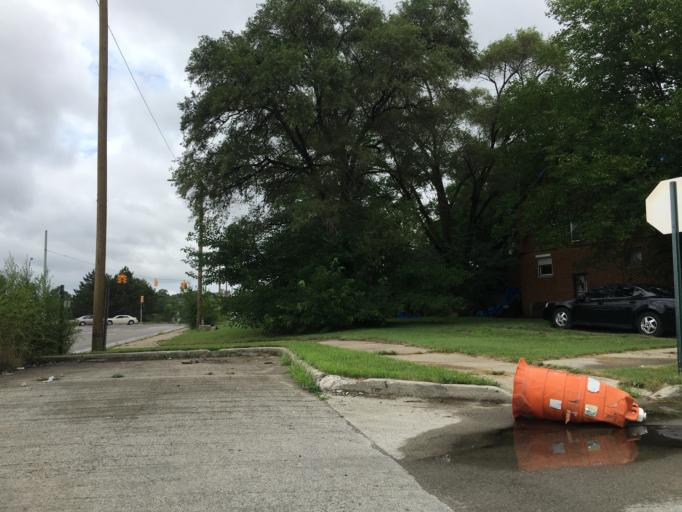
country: US
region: Michigan
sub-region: Oakland County
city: Oak Park
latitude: 42.4054
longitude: -83.1587
